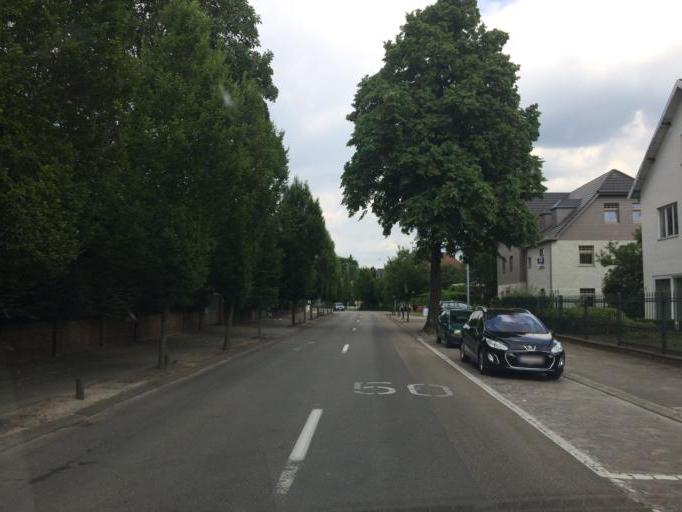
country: BE
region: Flanders
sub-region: Provincie Antwerpen
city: Mol
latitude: 51.1954
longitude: 5.1162
